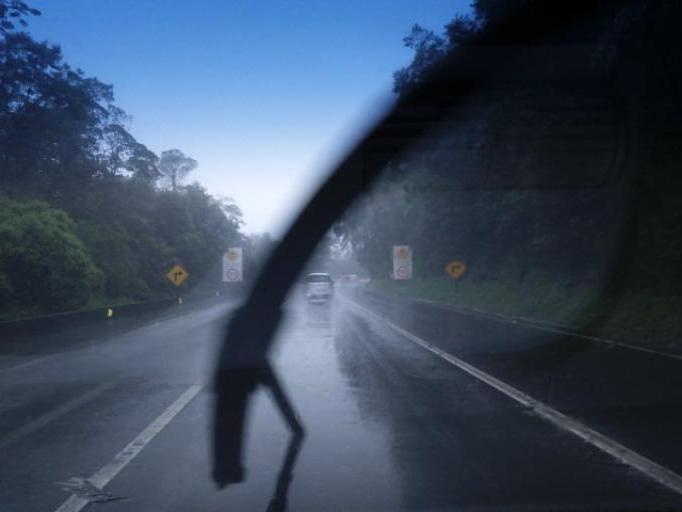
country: BR
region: Parana
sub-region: Guaratuba
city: Guaratuba
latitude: -25.8625
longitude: -48.9398
